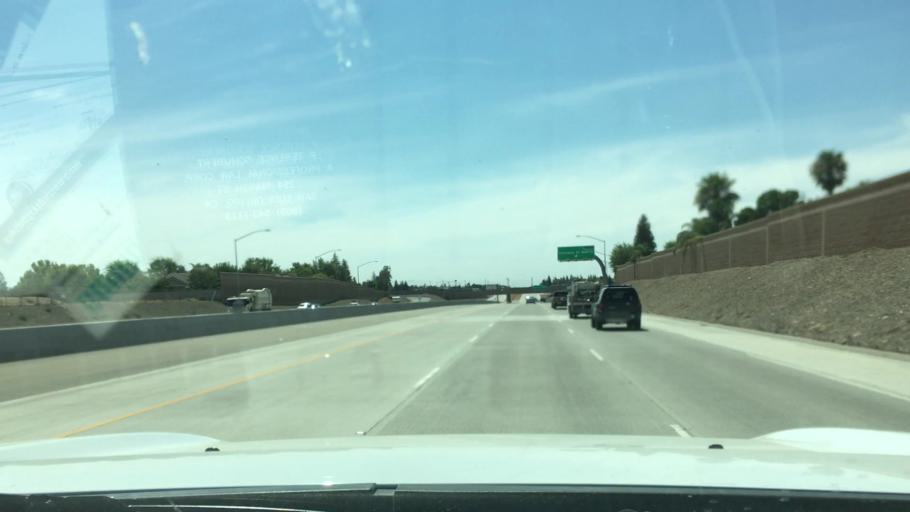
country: US
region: California
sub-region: Kern County
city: Greenacres
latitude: 35.3620
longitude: -119.1094
